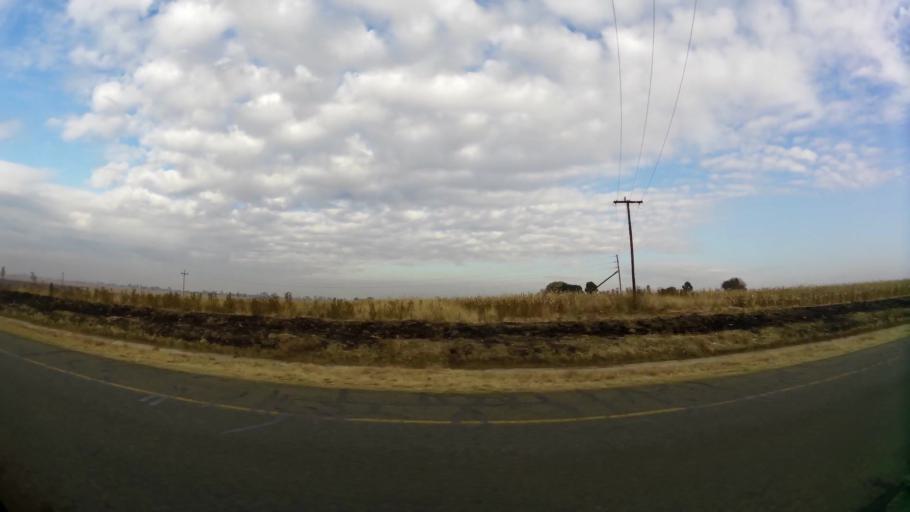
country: ZA
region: Gauteng
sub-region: Sedibeng District Municipality
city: Vanderbijlpark
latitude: -26.6491
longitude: 27.7796
